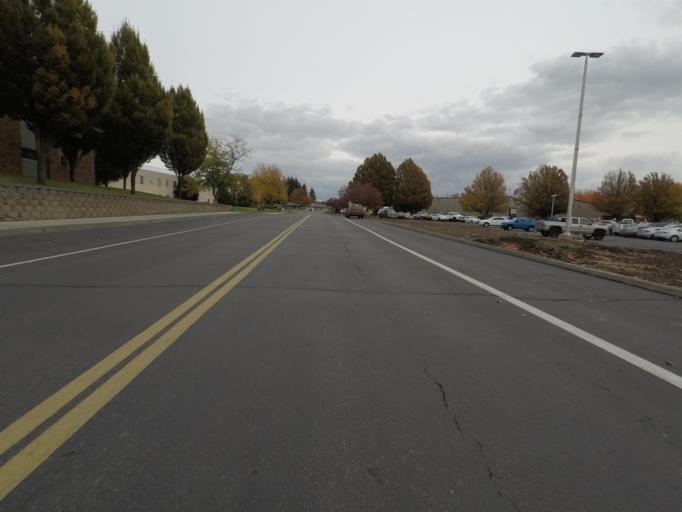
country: US
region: Washington
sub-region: Walla Walla County
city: Walla Walla East
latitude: 46.0801
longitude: -118.2771
